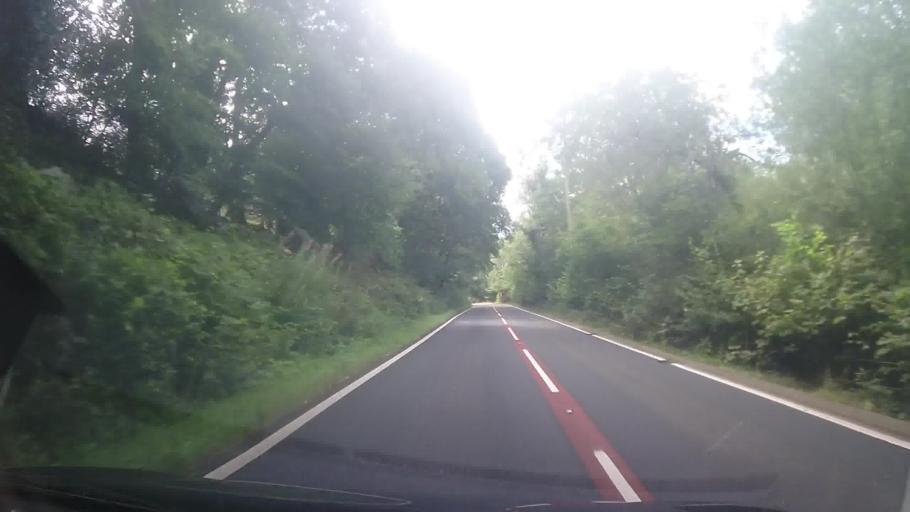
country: GB
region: Wales
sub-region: Sir Powys
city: Machynlleth
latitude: 52.5670
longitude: -3.9135
